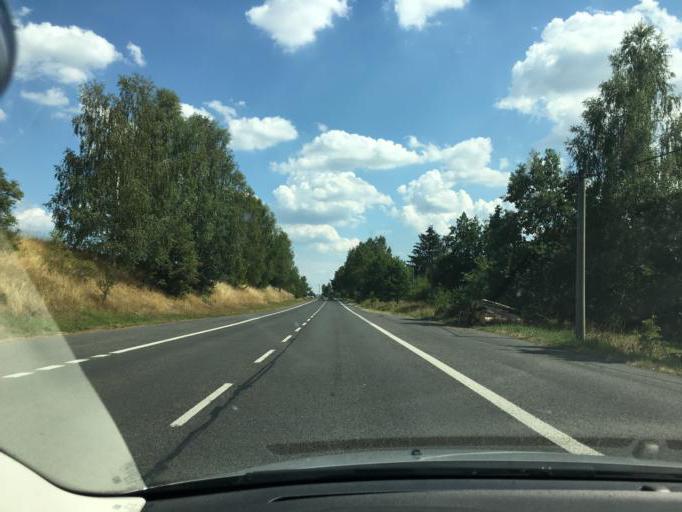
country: CZ
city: Jablonne v Podjestedi
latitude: 50.7731
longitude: 14.7242
